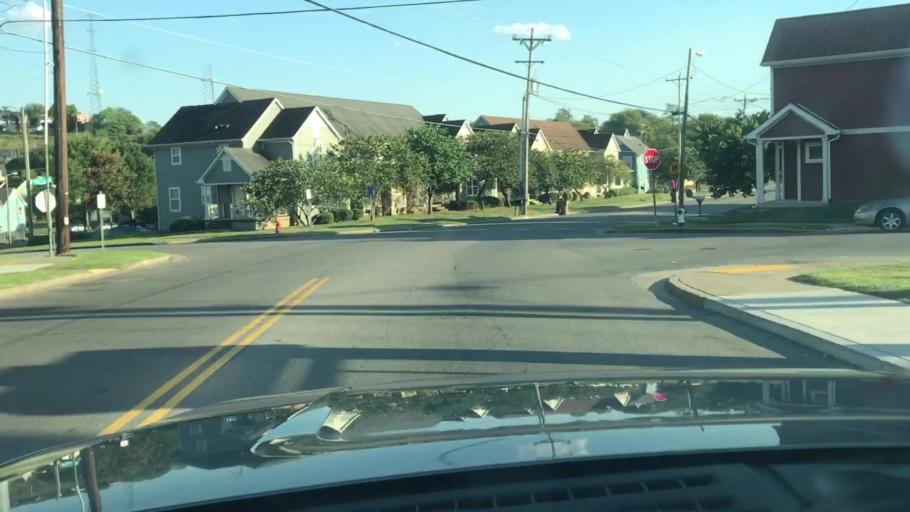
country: US
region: Tennessee
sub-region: Davidson County
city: Nashville
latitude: 36.1584
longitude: -86.8344
